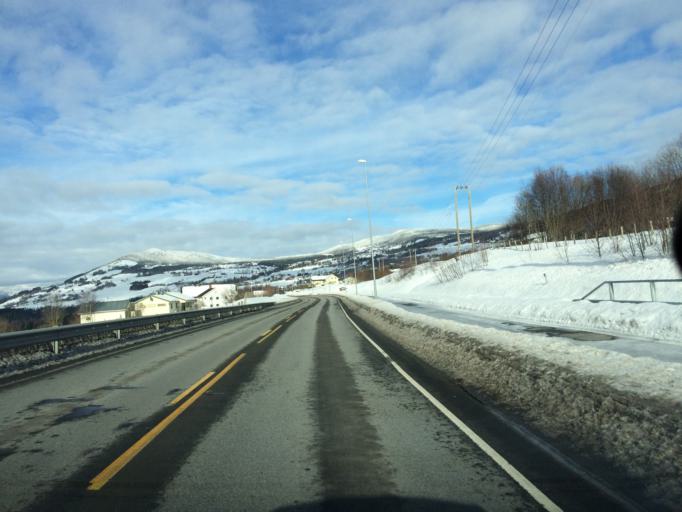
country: NO
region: Oppland
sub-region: Gausdal
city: Segalstad bru
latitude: 61.2001
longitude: 10.3061
